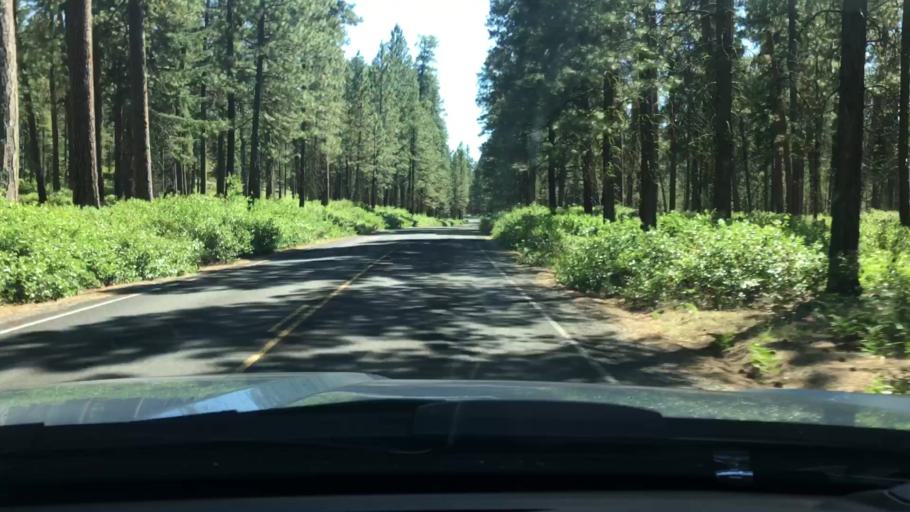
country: US
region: Oregon
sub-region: Deschutes County
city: Sisters
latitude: 44.4148
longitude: -121.6714
